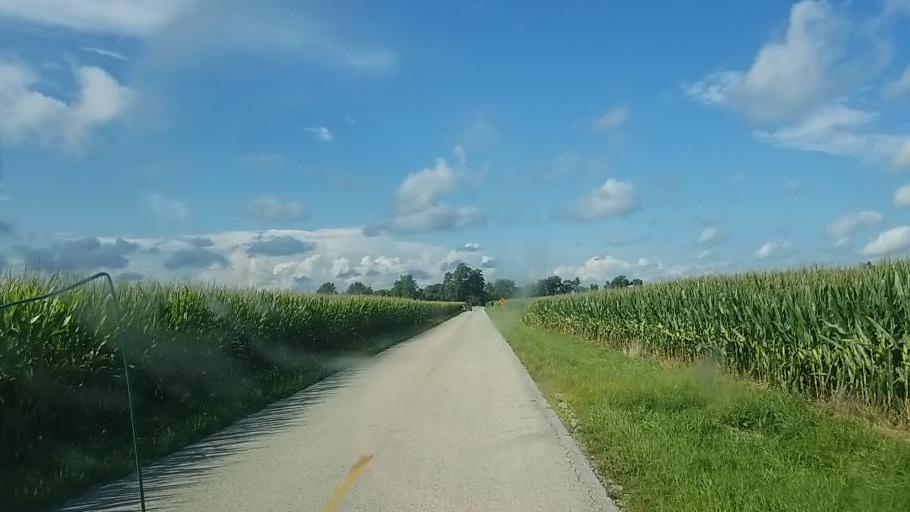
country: US
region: Ohio
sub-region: Hardin County
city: Forest
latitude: 40.7264
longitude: -83.5145
